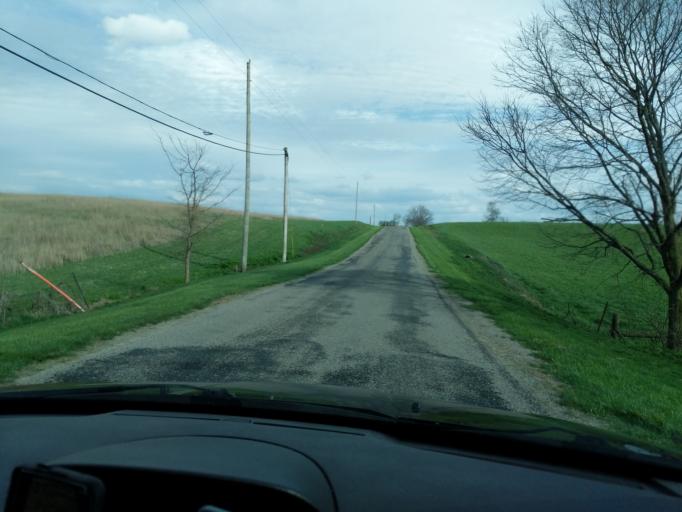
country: US
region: Ohio
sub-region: Champaign County
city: North Lewisburg
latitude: 40.1967
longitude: -83.6567
